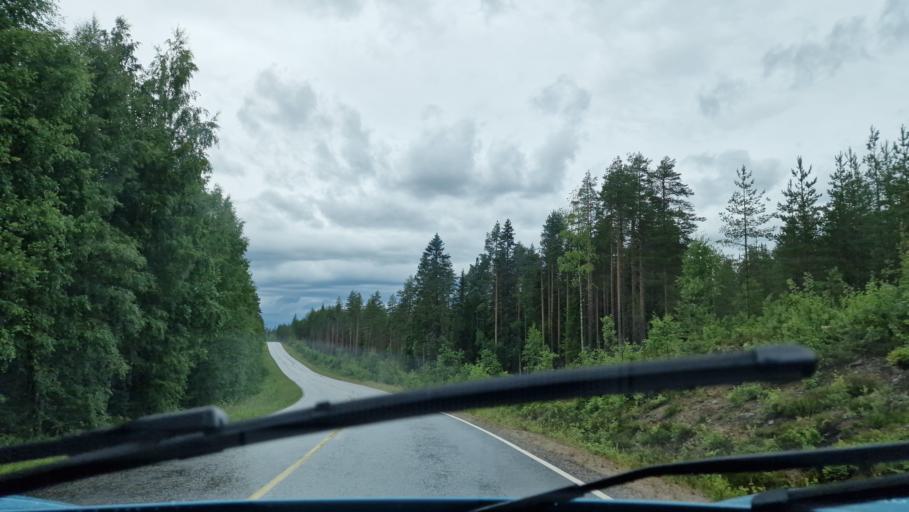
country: FI
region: Central Finland
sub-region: Saarijaervi-Viitasaari
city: Pylkoenmaeki
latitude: 62.6683
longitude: 24.5346
